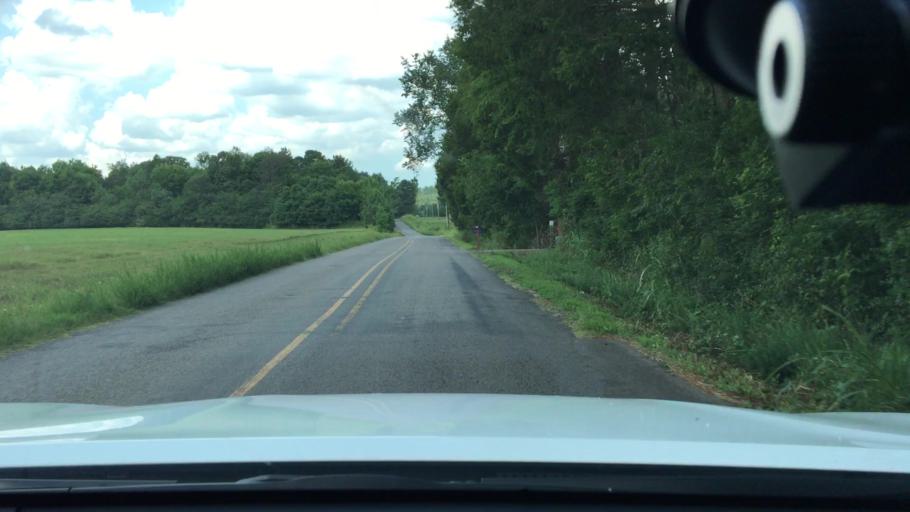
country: US
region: Arkansas
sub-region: Logan County
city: Paris
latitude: 35.2691
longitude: -93.6761
